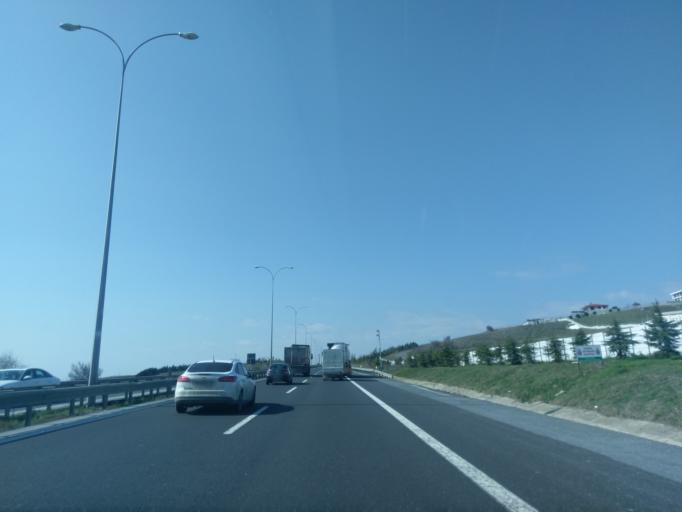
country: TR
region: Istanbul
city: Celaliye
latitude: 41.0670
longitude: 28.3947
